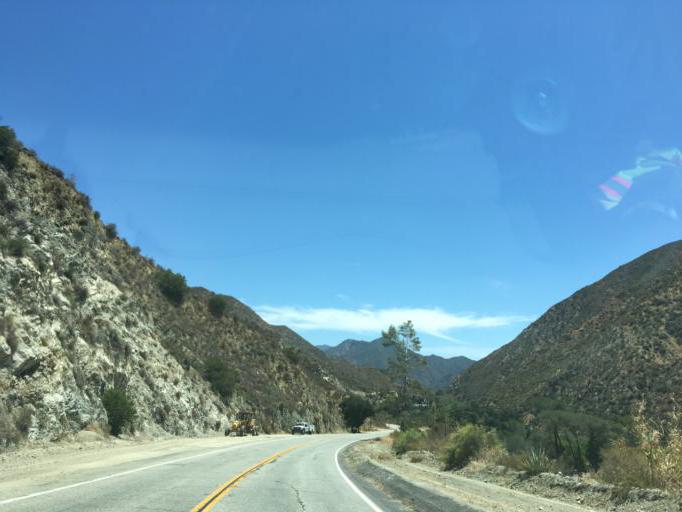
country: US
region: California
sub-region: Los Angeles County
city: La Crescenta-Montrose
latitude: 34.3047
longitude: -118.2602
